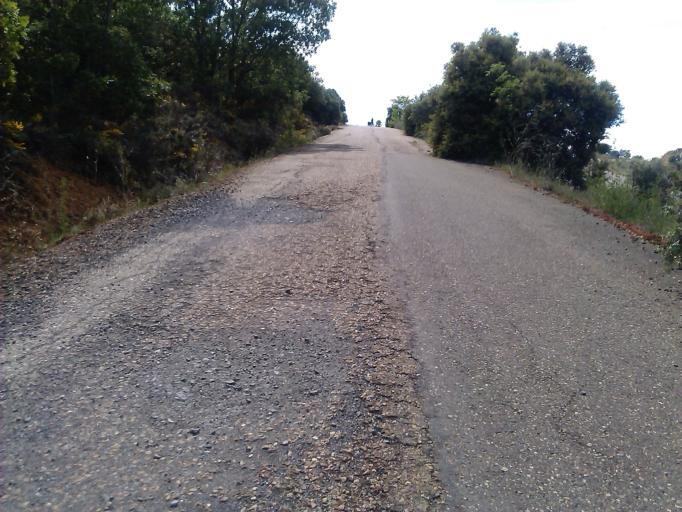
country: ES
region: Castille and Leon
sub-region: Provincia de Leon
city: San Justo de la Vega
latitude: 42.4481
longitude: -5.9793
